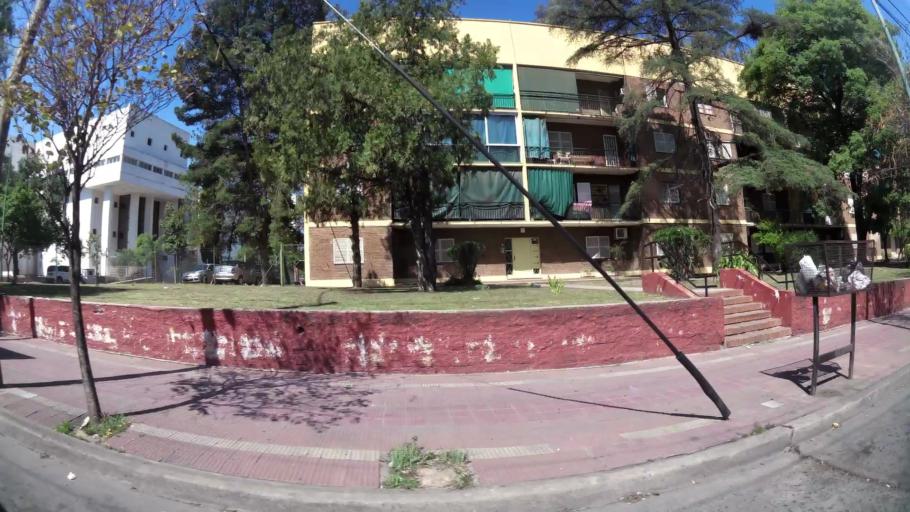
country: AR
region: Cordoba
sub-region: Departamento de Capital
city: Cordoba
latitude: -31.4073
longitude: -64.1585
